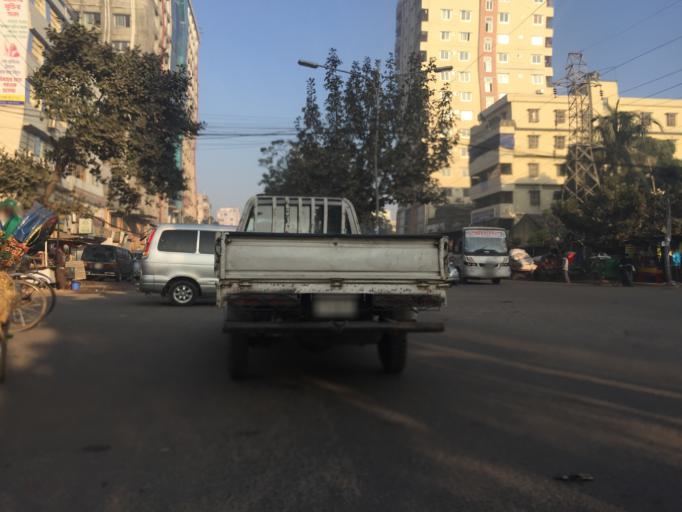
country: BD
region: Dhaka
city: Azimpur
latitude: 23.8023
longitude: 90.3536
